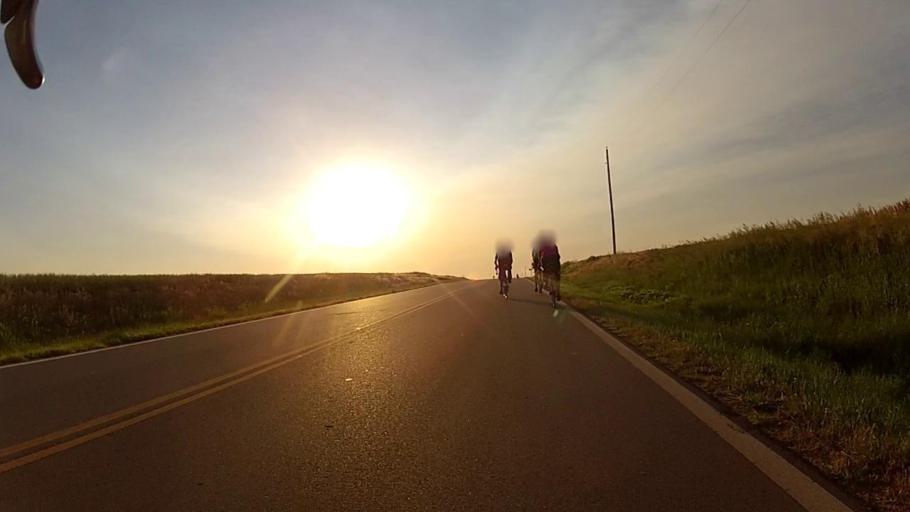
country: US
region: Kansas
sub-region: Harper County
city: Anthony
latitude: 37.1528
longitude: -97.9293
